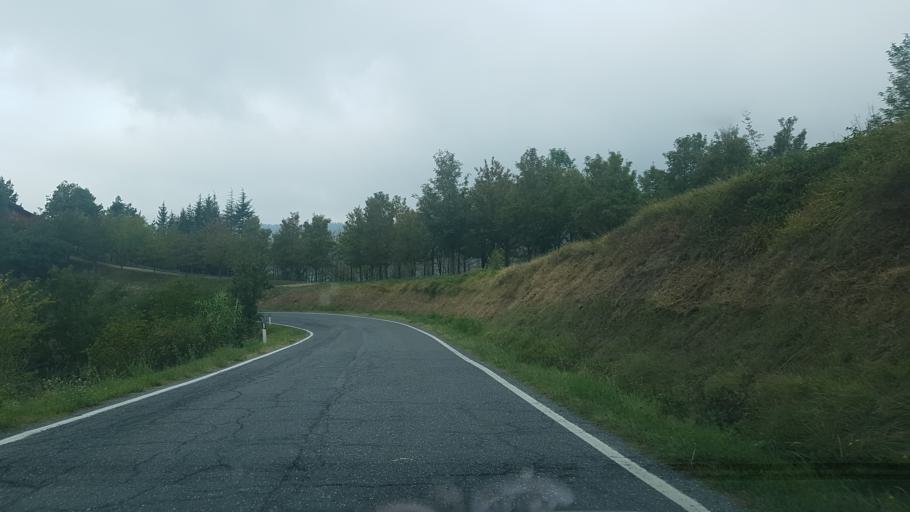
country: IT
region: Piedmont
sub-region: Provincia di Cuneo
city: Paroldo
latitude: 44.4322
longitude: 8.0801
